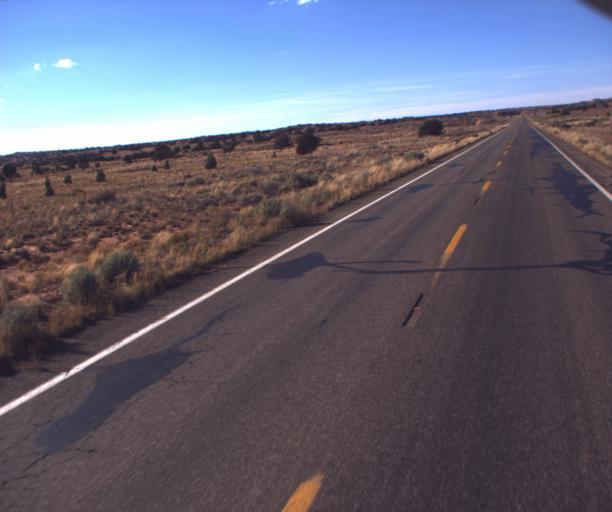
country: US
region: Arizona
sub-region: Coconino County
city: Kaibito
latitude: 36.6111
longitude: -111.1853
